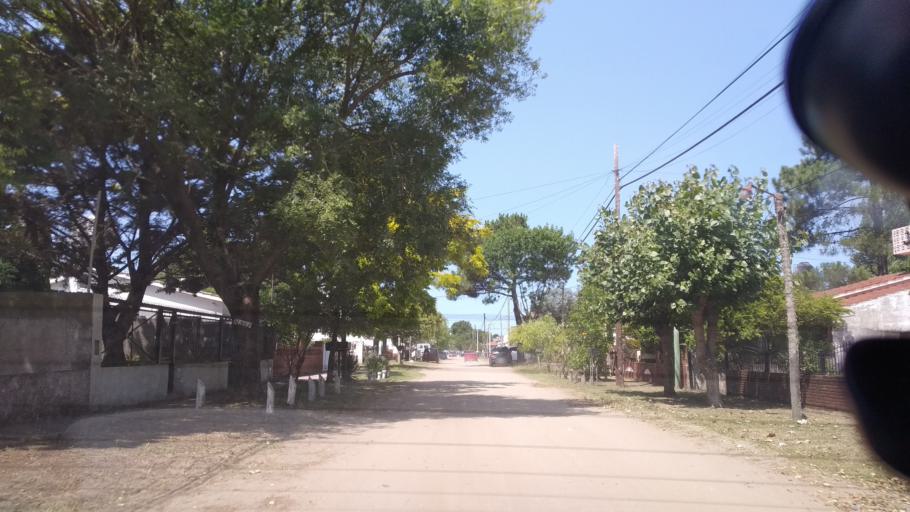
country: AR
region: Buenos Aires
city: Mar del Tuyu
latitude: -36.5835
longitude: -56.6929
